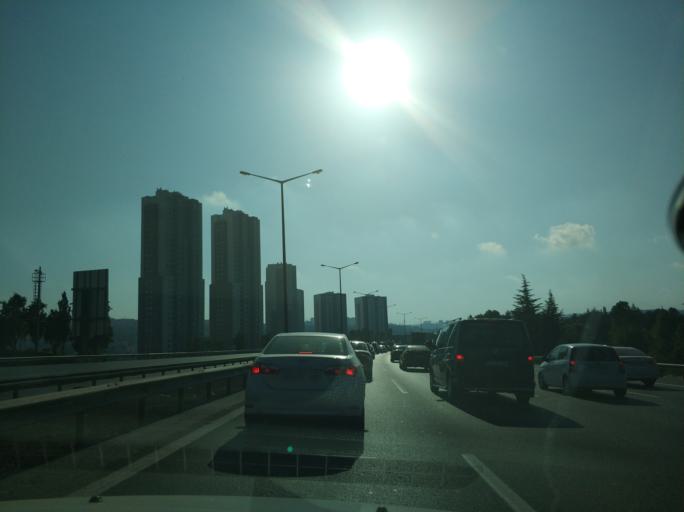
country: TR
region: Istanbul
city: Sisli
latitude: 41.0918
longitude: 28.9428
